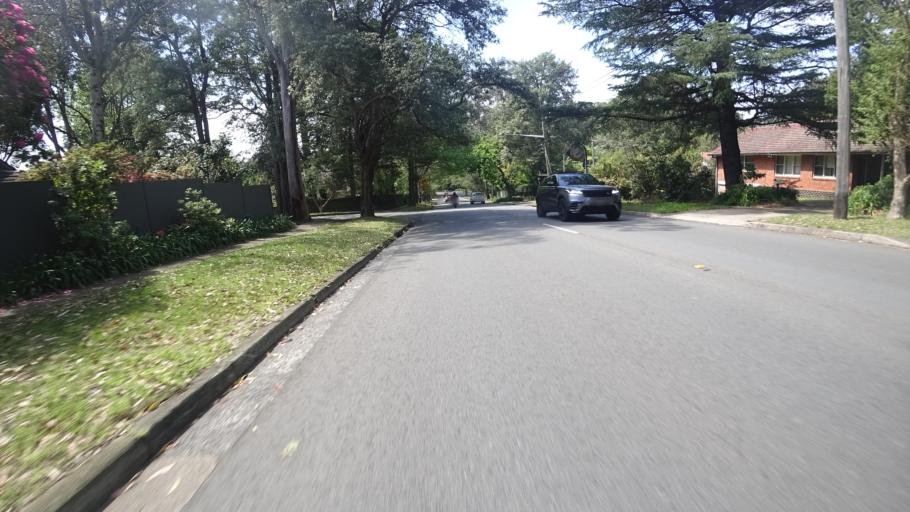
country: AU
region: New South Wales
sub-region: City of Sydney
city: North Turramurra
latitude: -33.7160
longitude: 151.1368
